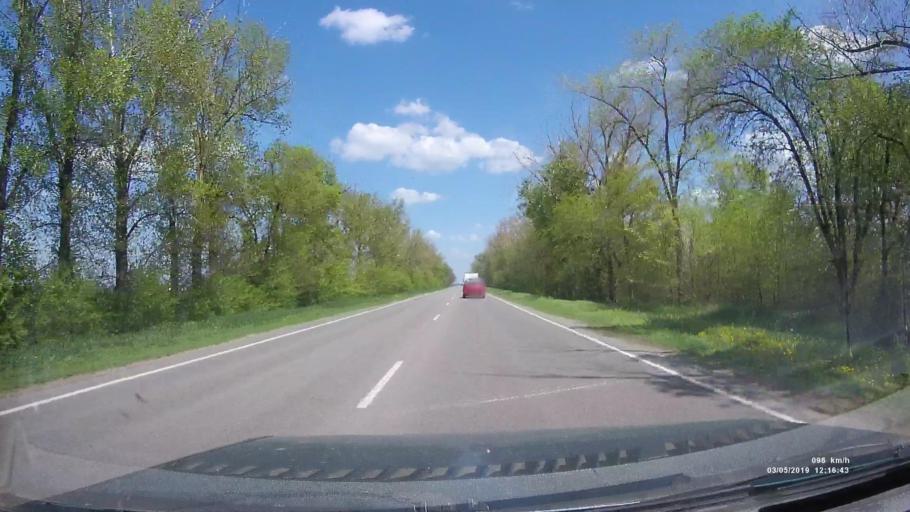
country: RU
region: Rostov
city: Melikhovskaya
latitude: 47.3753
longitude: 40.5868
